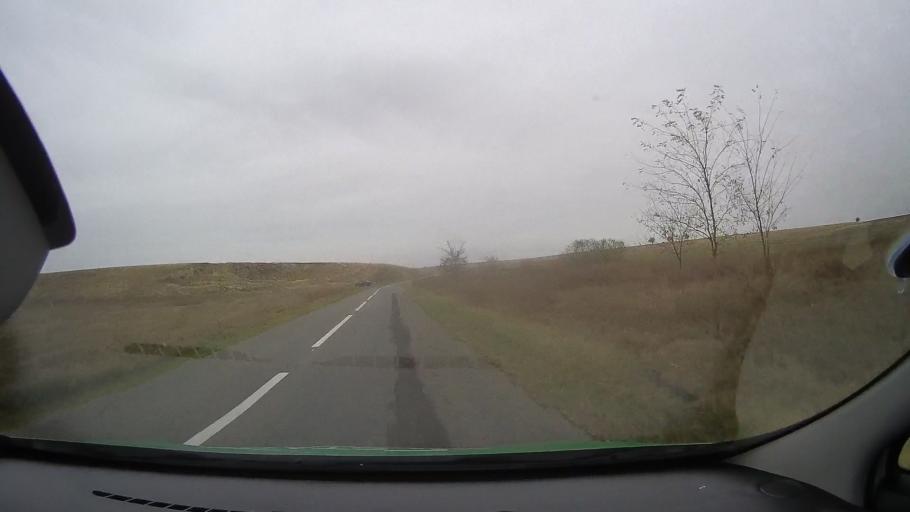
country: RO
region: Constanta
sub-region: Comuna Saraiu
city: Saraiu
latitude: 44.7267
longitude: 28.1761
